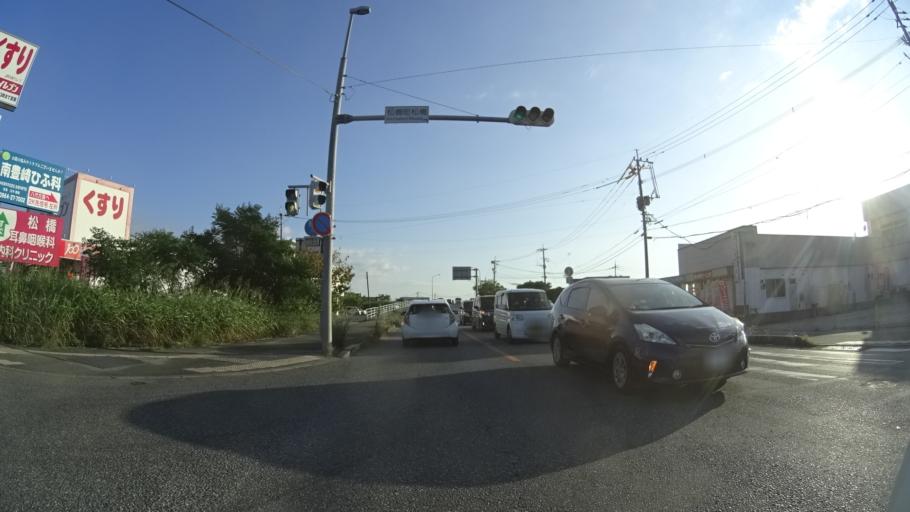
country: JP
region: Kumamoto
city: Matsubase
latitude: 32.6468
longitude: 130.6765
